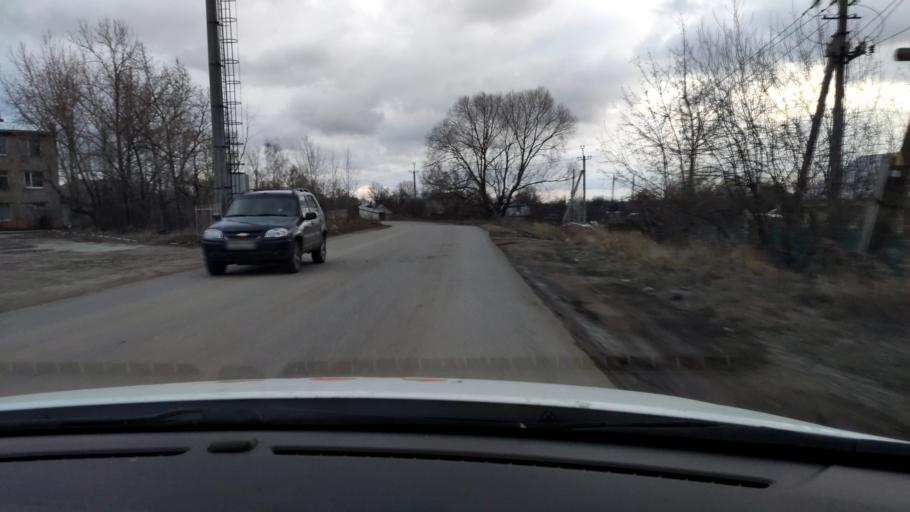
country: RU
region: Tatarstan
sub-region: Gorod Kazan'
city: Kazan
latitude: 55.7220
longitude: 49.0934
